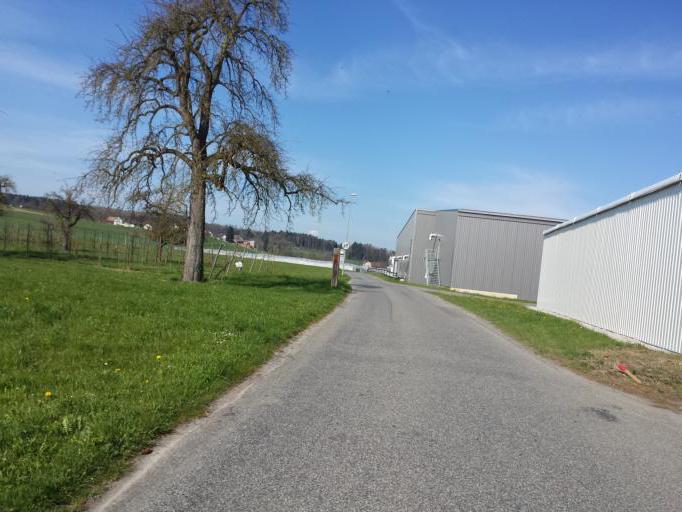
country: CH
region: Saint Gallen
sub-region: Wahlkreis St. Gallen
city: Muolen
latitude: 47.5345
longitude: 9.3404
